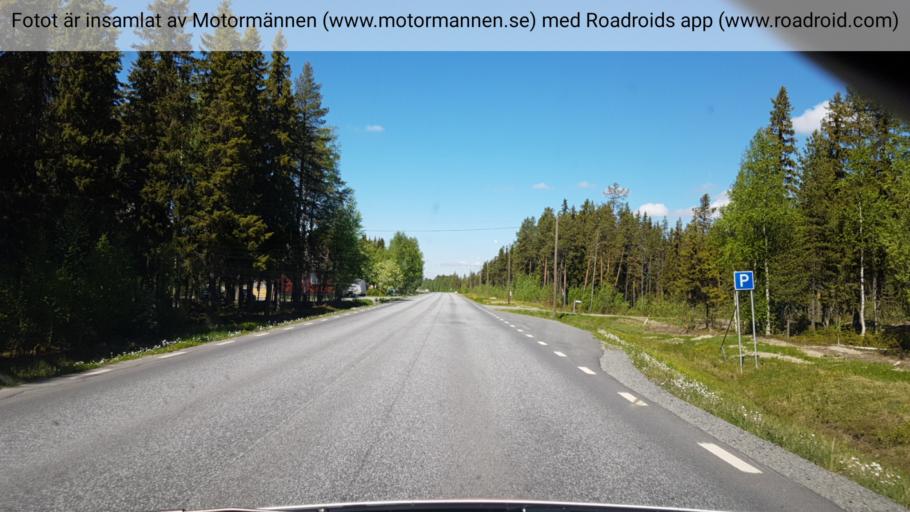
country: SE
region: Vaesterbotten
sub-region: Vilhelmina Kommun
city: Vilhelmina
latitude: 64.5952
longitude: 16.7284
